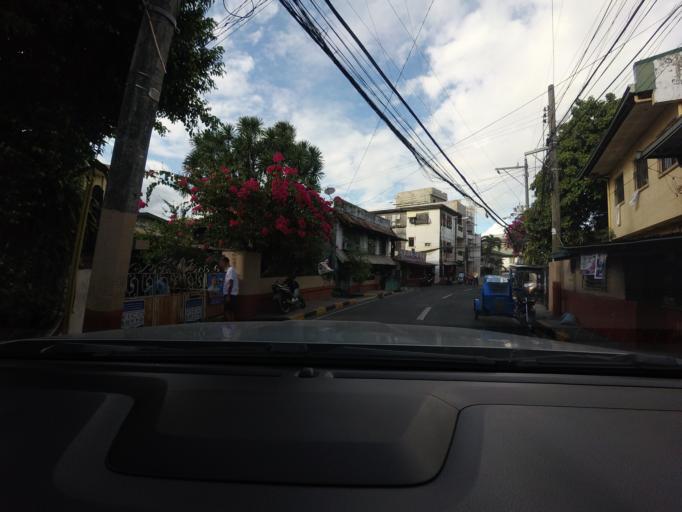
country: PH
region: Calabarzon
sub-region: Province of Rizal
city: Pateros
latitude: 14.5644
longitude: 121.0784
